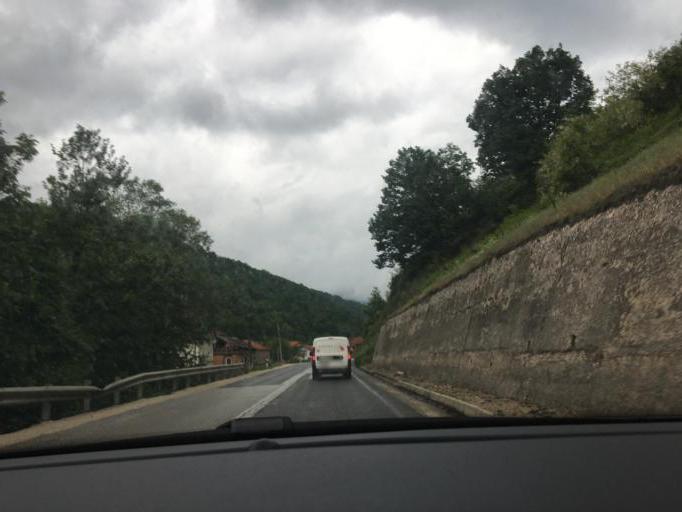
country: MK
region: Kicevo
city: Zajas
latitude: 41.6374
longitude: 20.9016
